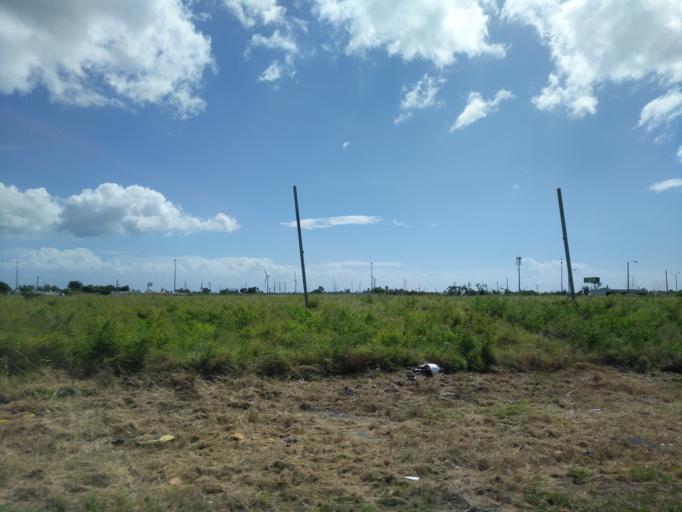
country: PR
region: Santa Isabel Municipio
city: El Ojo
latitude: 18.0146
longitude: -66.3810
